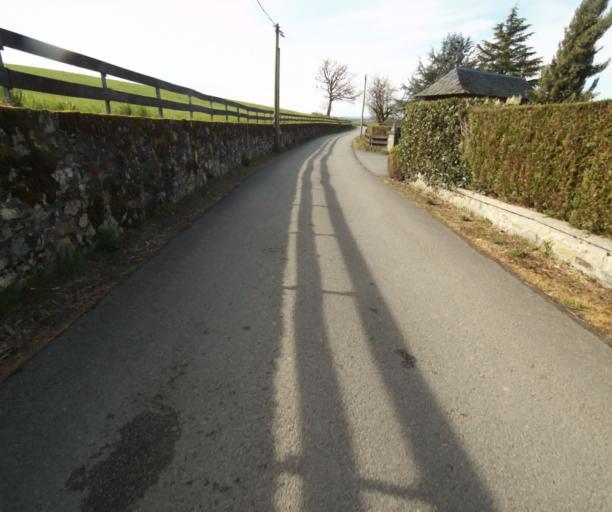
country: FR
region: Limousin
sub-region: Departement de la Correze
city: Correze
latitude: 45.3382
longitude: 1.8296
